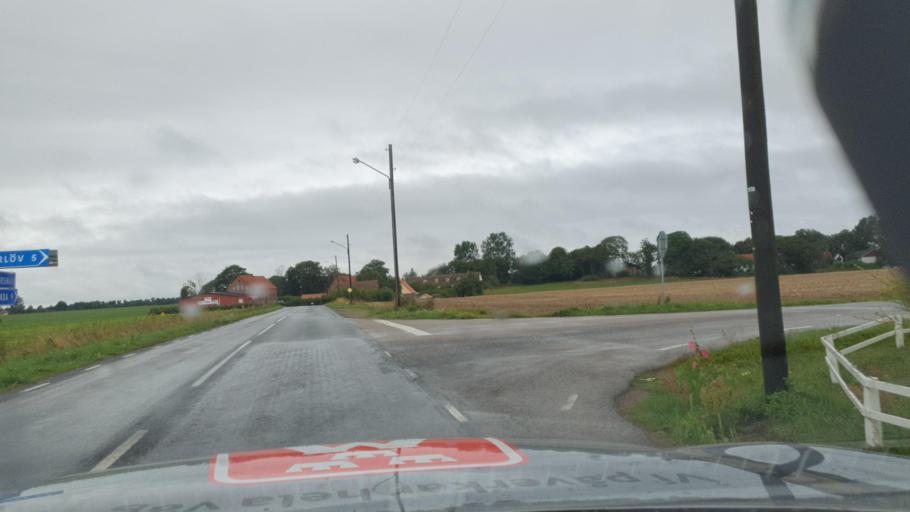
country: SE
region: Skane
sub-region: Simrishamns Kommun
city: Kivik
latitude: 55.5646
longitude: 14.1563
